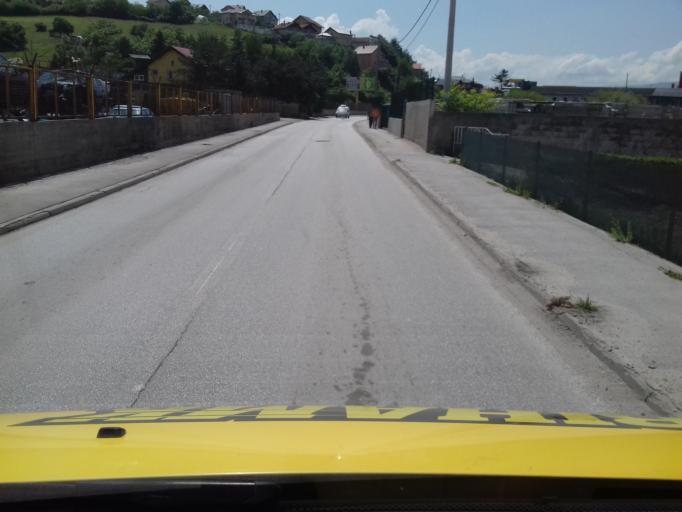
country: BA
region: Federation of Bosnia and Herzegovina
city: Vogosca
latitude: 43.8747
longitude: 18.3100
